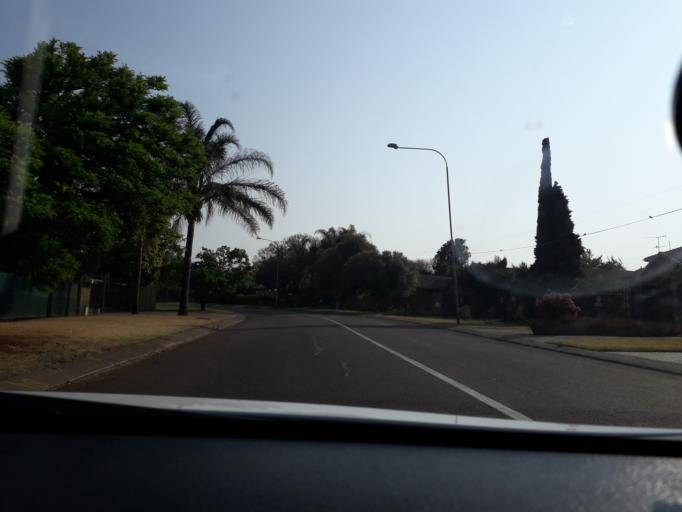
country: ZA
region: Gauteng
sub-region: City of Tshwane Metropolitan Municipality
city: Centurion
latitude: -25.8691
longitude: 28.1754
